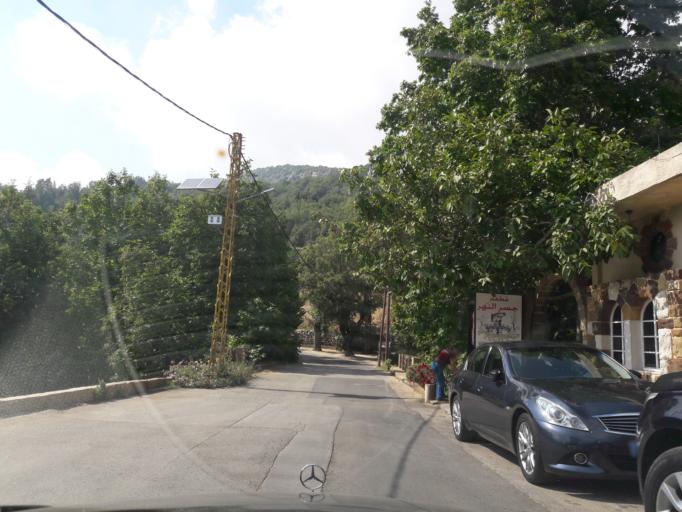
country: LB
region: Mont-Liban
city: Djounie
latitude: 33.9632
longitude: 35.7802
